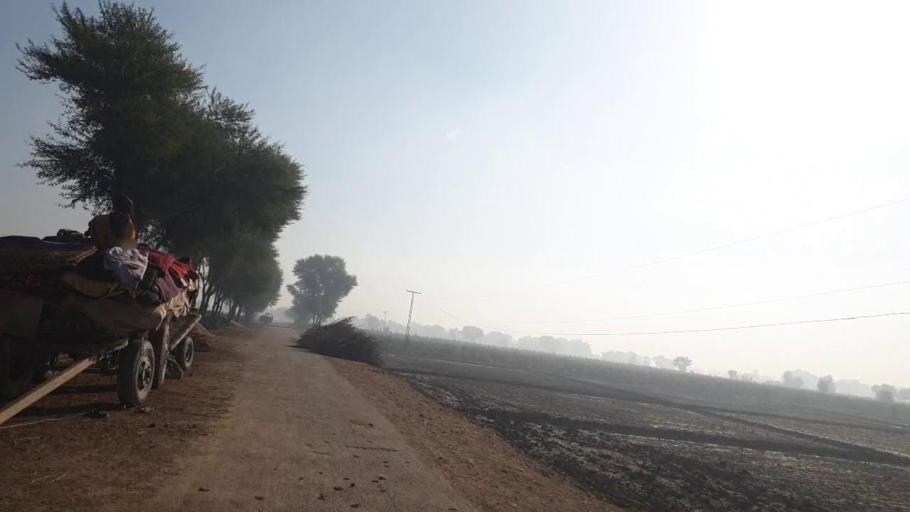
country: PK
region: Sindh
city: Dadu
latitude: 26.6742
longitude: 67.8036
